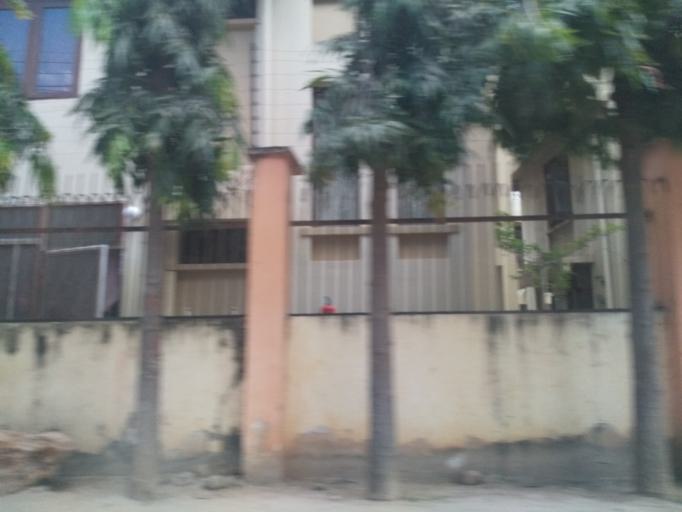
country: TZ
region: Dar es Salaam
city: Magomeni
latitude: -6.7636
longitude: 39.2677
